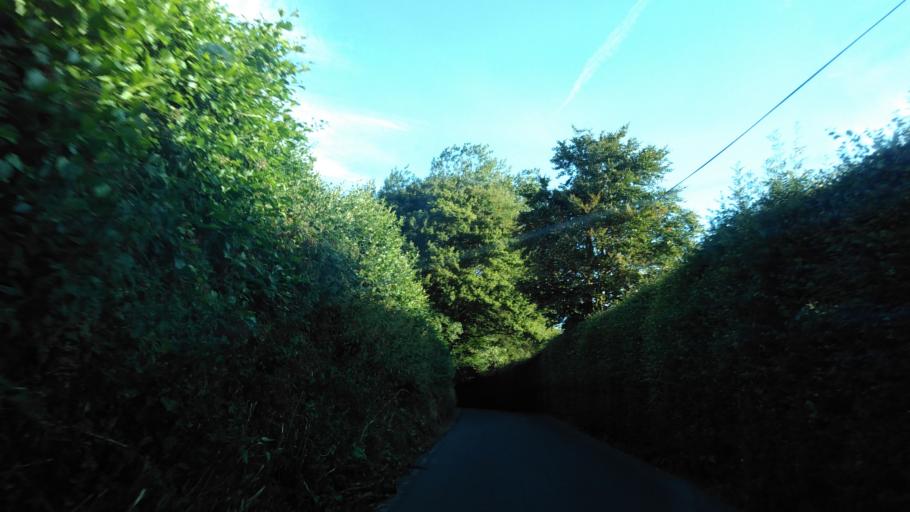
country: GB
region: England
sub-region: Kent
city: Chartham
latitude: 51.2774
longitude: 1.0111
